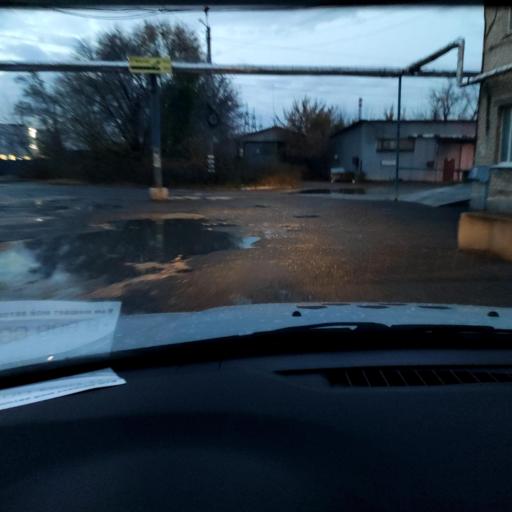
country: RU
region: Samara
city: Zhigulevsk
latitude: 53.5199
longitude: 49.4747
